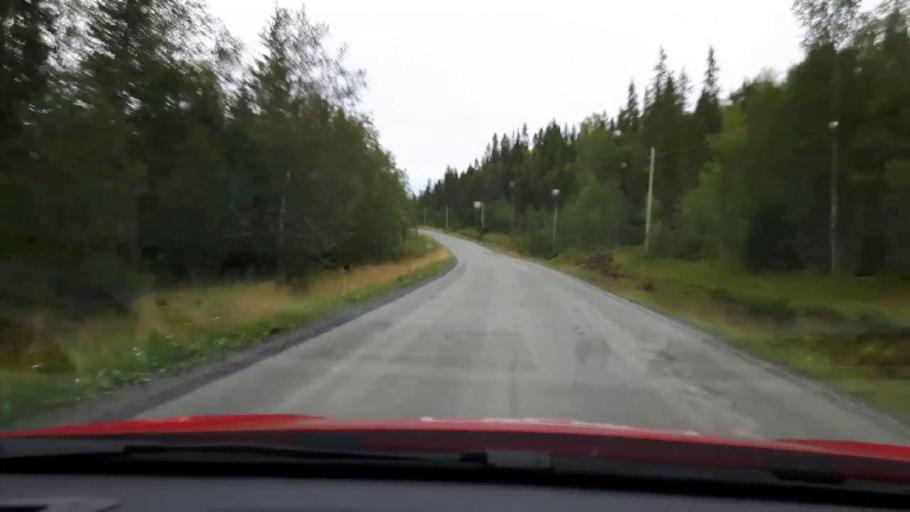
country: SE
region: Jaemtland
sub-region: Are Kommun
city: Jarpen
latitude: 63.4288
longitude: 13.3188
